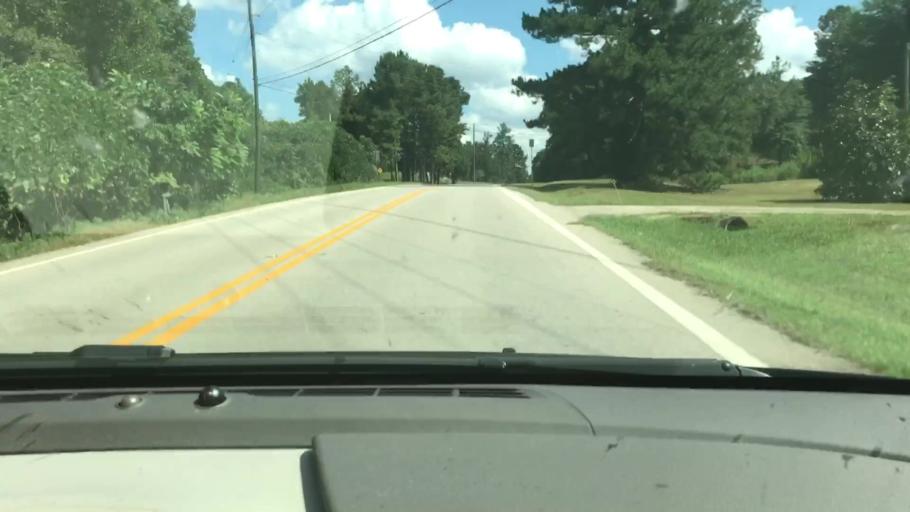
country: US
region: Georgia
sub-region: Troup County
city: La Grange
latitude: 32.8981
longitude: -85.0303
